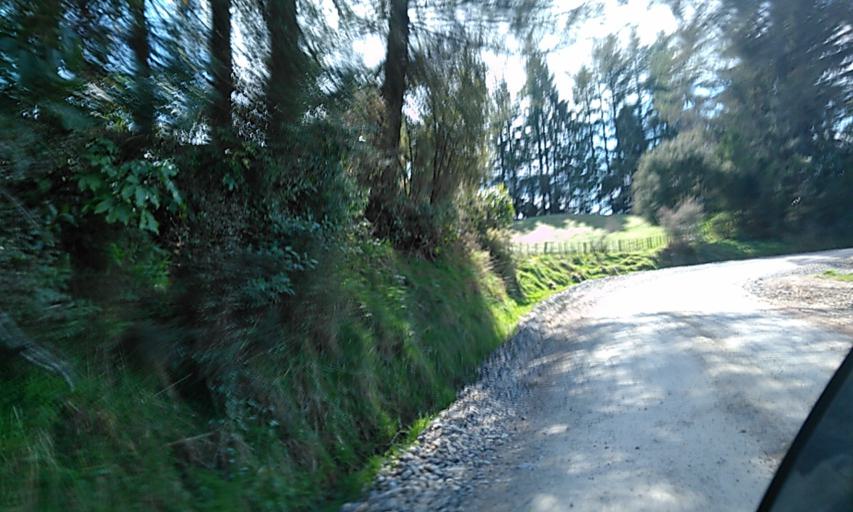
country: NZ
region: Gisborne
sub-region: Gisborne District
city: Gisborne
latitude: -38.2106
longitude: 178.0653
